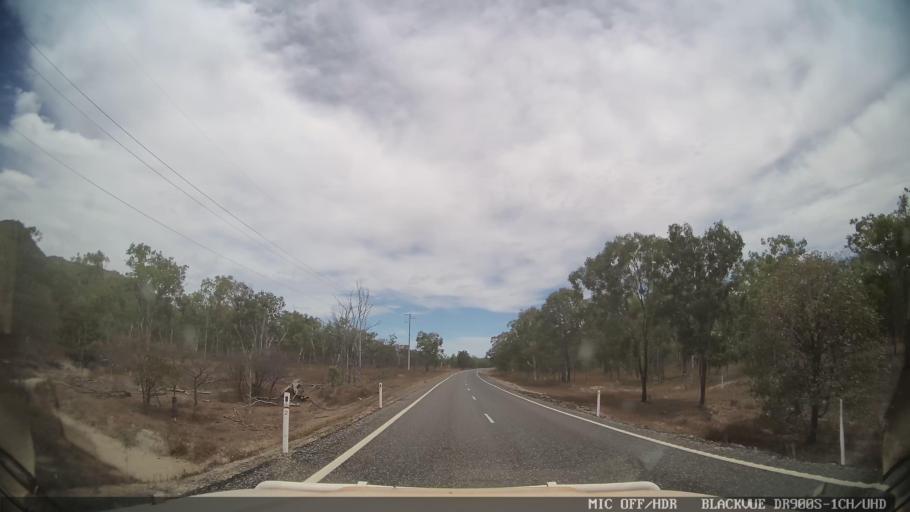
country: AU
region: Queensland
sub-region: Cairns
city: Port Douglas
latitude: -16.2497
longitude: 144.7262
